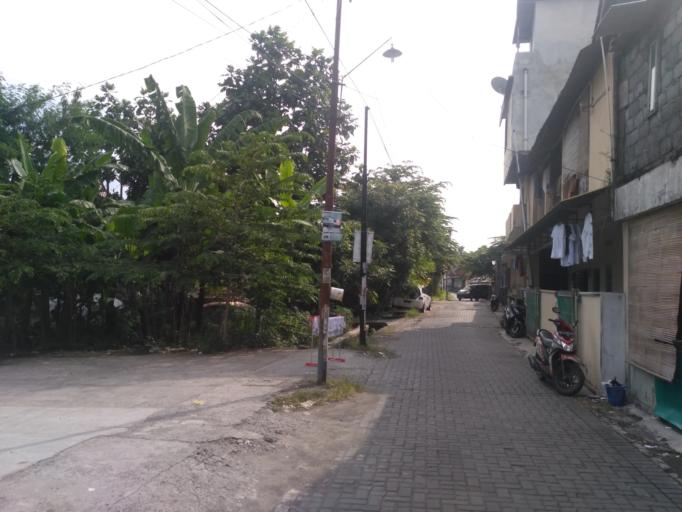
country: ID
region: Daerah Istimewa Yogyakarta
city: Depok
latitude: -7.7746
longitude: 110.4086
